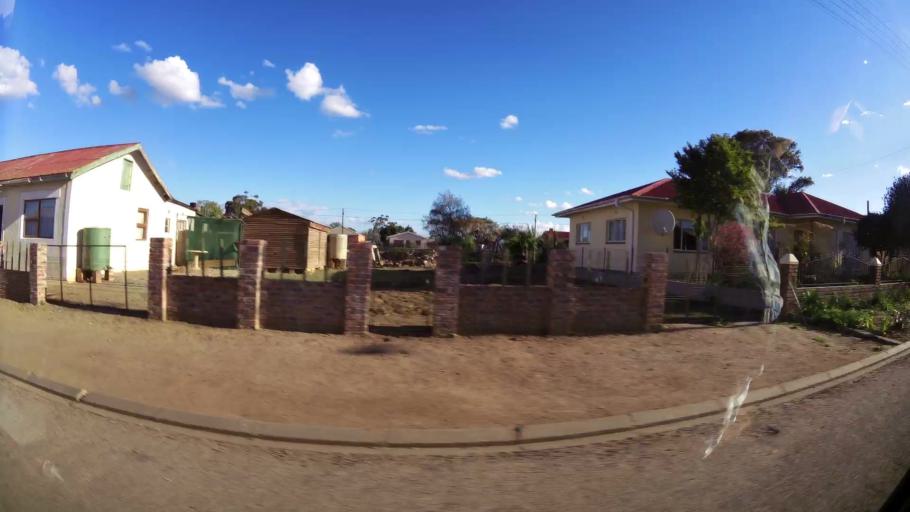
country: ZA
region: Western Cape
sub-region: Eden District Municipality
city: Riversdale
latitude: -34.0999
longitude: 20.9635
